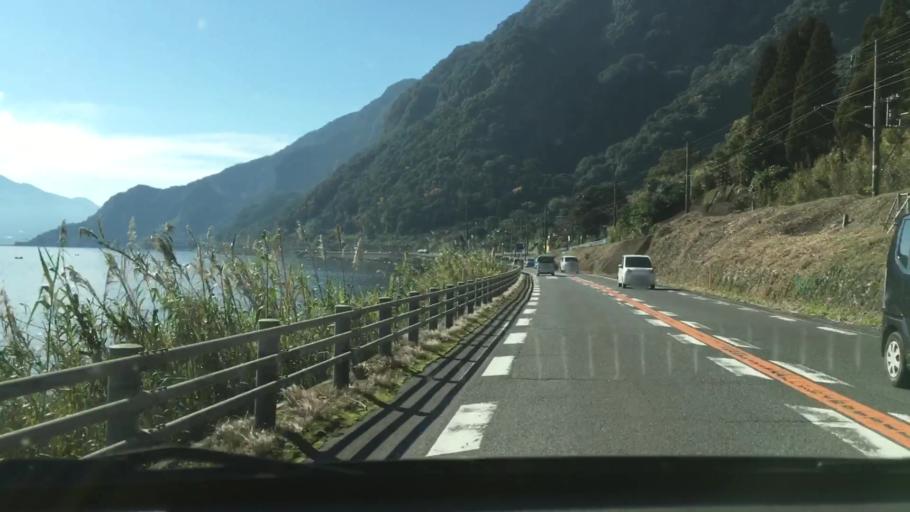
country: JP
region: Kagoshima
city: Kajiki
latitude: 31.6847
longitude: 130.6099
